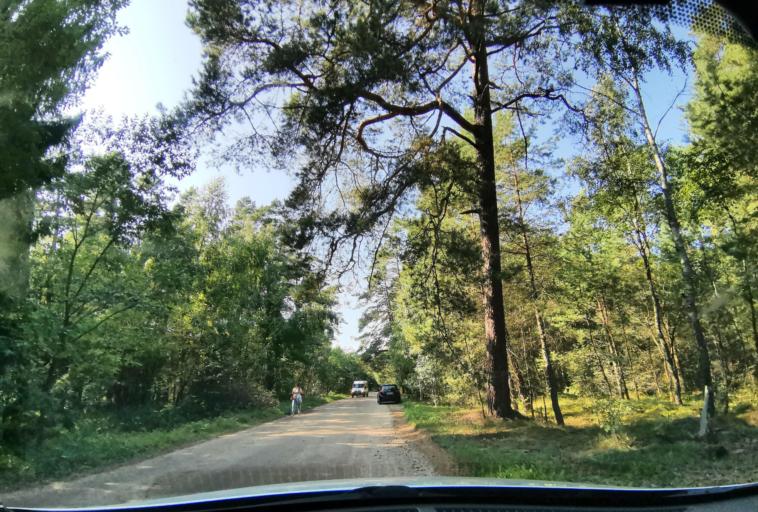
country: LT
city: Nida
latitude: 55.1613
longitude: 20.8296
